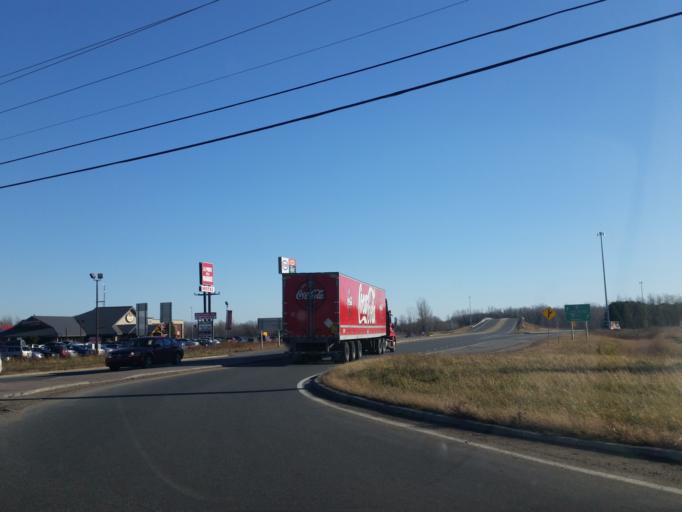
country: CA
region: Quebec
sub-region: Mauricie
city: Yamachiche
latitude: 46.2622
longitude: -72.8779
